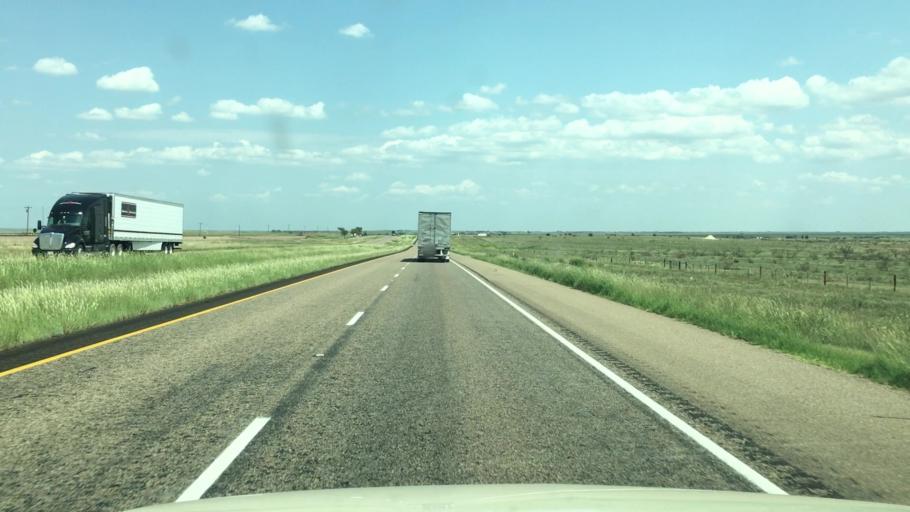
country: US
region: Texas
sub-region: Armstrong County
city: Claude
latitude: 35.0325
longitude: -101.1450
